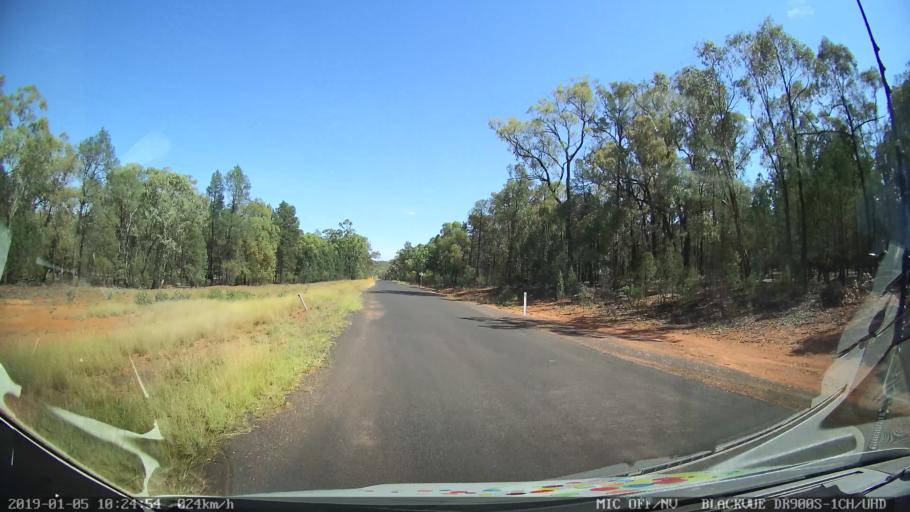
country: AU
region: New South Wales
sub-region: Gilgandra
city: Gilgandra
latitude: -31.5648
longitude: 148.9612
